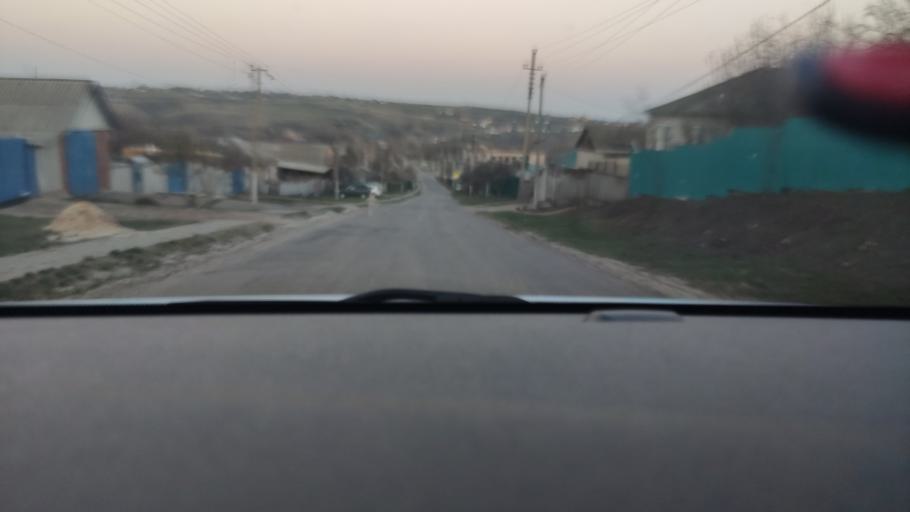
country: RU
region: Voronezj
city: Uryv-Pokrovka
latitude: 51.1119
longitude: 39.1556
